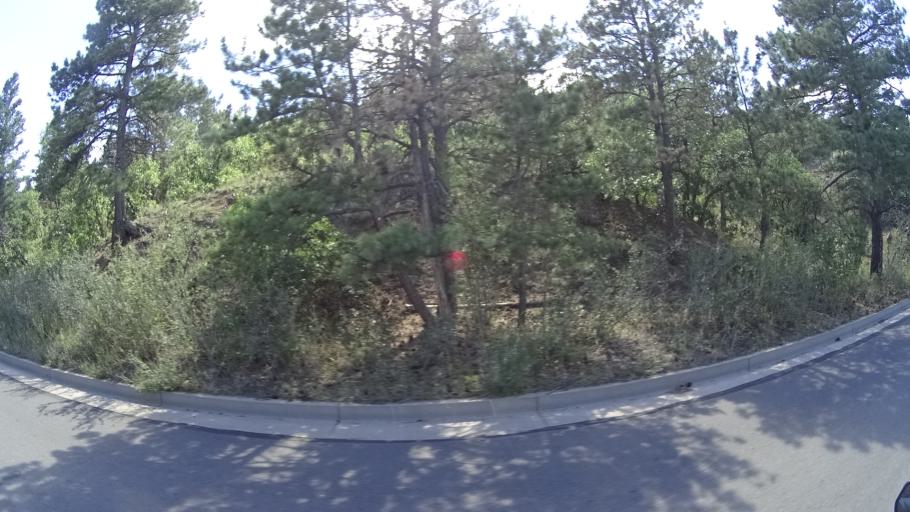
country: US
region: Colorado
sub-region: El Paso County
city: Manitou Springs
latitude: 38.8184
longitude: -104.8827
